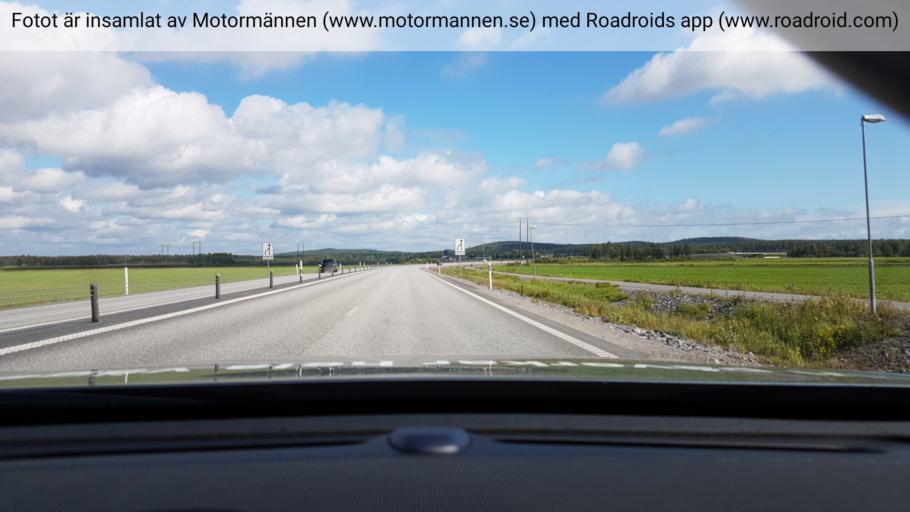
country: SE
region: Vaesterbotten
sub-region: Umea Kommun
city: Roback
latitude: 63.8488
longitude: 20.1908
